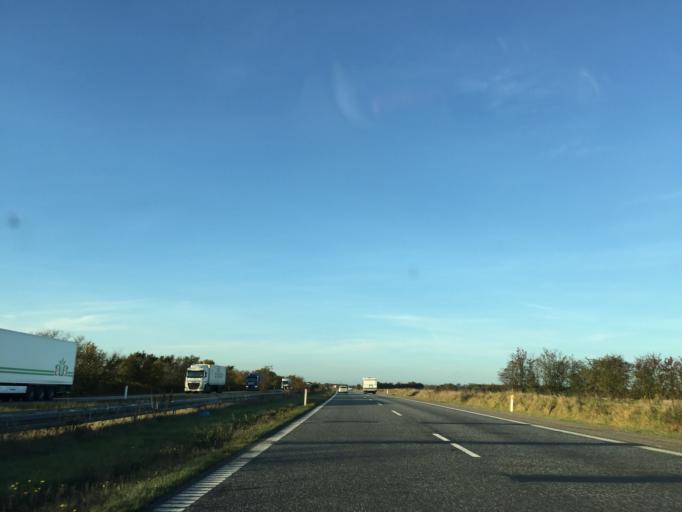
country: DK
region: South Denmark
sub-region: Aabenraa Kommune
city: Krusa
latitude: 54.8857
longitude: 9.3786
